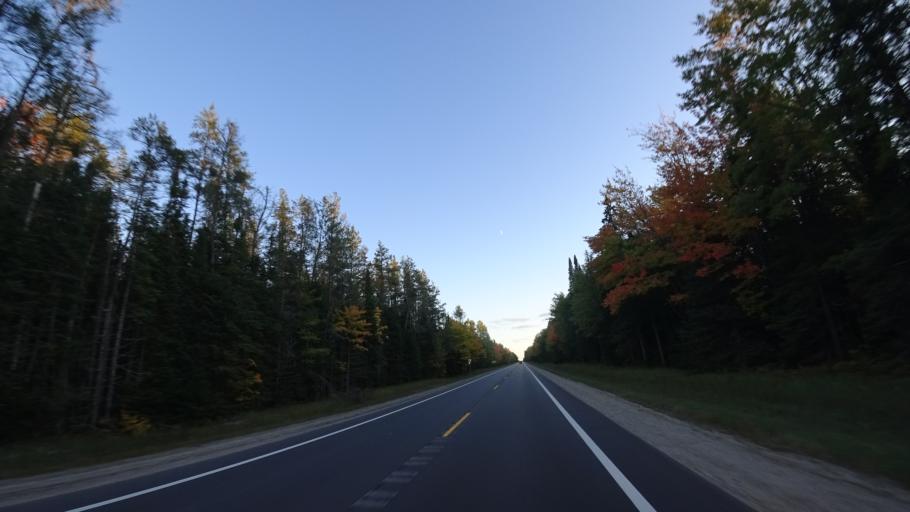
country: US
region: Michigan
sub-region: Mackinac County
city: Saint Ignace
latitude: 46.2754
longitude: -85.0095
